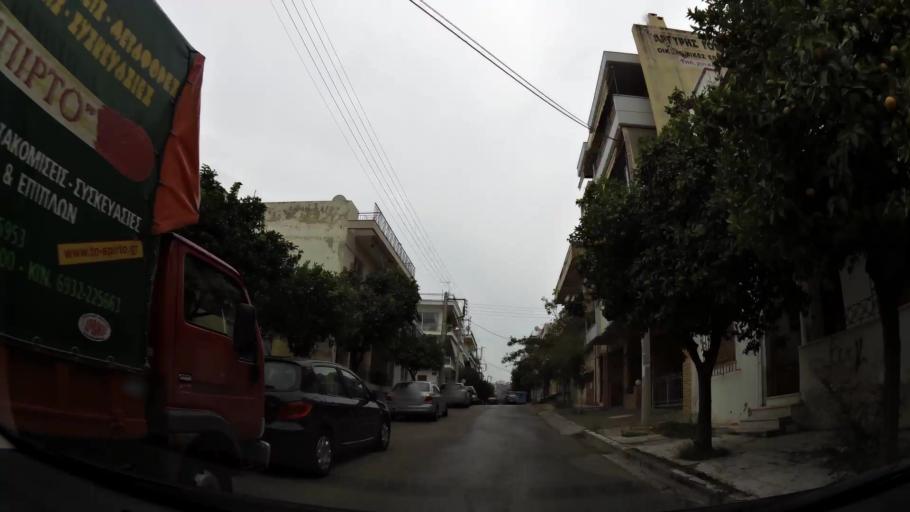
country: GR
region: Attica
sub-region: Nomos Piraios
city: Korydallos
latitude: 37.9835
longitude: 23.6531
